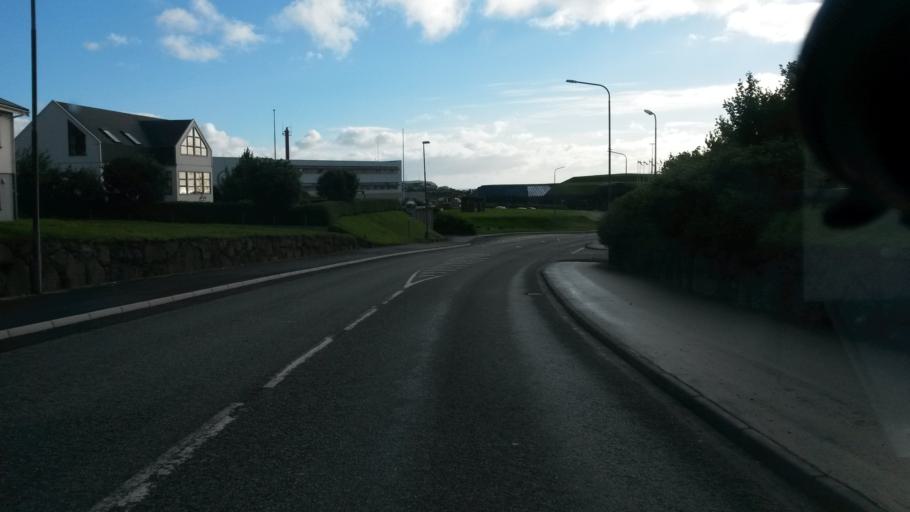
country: FO
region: Streymoy
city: Hoyvik
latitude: 62.0213
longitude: -6.7882
